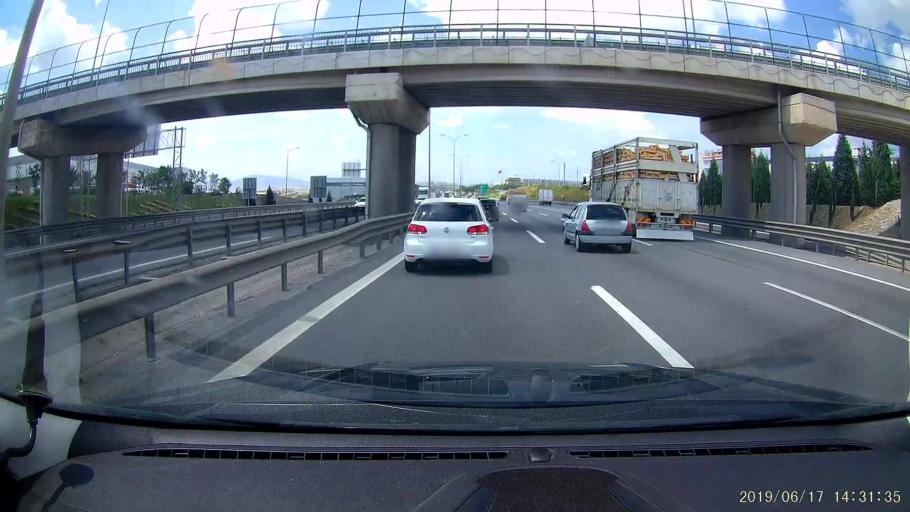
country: TR
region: Kocaeli
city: Balcik
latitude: 40.8546
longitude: 29.4090
